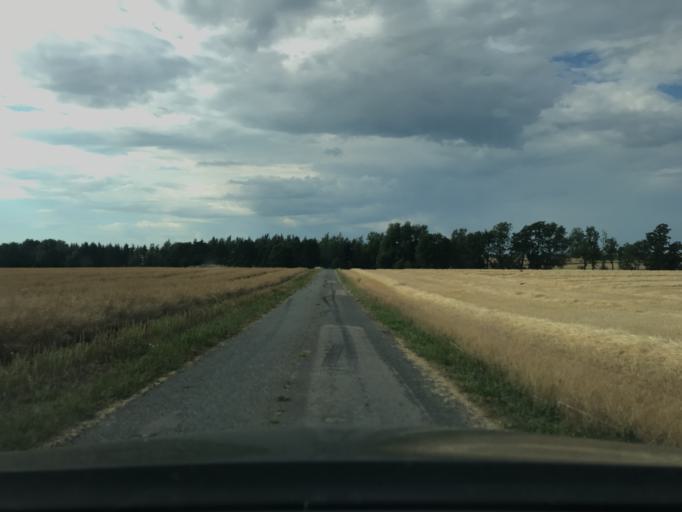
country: SE
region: Skane
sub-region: Simrishamns Kommun
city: Kivik
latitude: 55.5393
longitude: 14.1534
